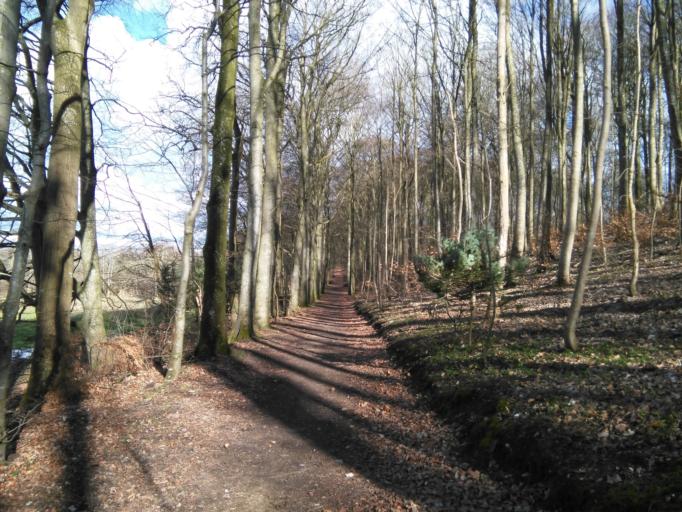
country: DK
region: Central Jutland
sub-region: Arhus Kommune
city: Beder
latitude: 56.0719
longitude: 10.2078
